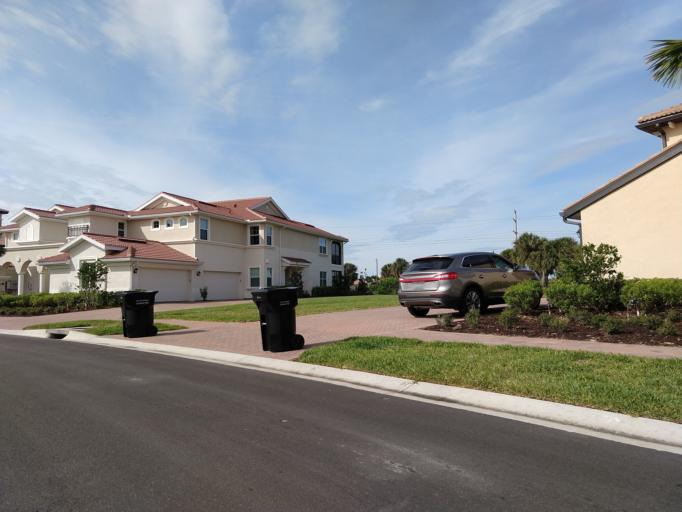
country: US
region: Florida
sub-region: Sarasota County
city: Nokomis
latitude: 27.1509
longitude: -82.3711
